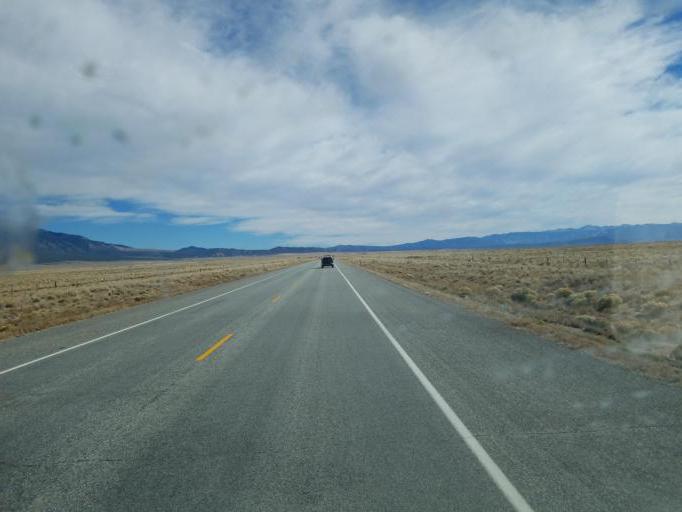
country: US
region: Colorado
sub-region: Alamosa County
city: Alamosa East
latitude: 37.4750
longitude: -105.6320
